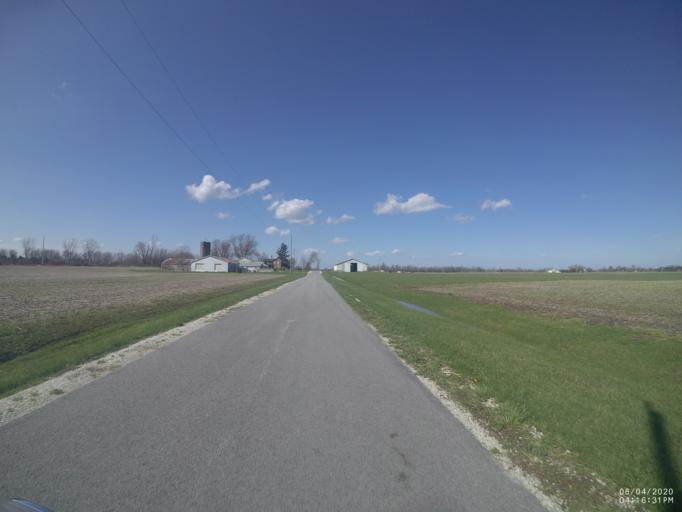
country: US
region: Ohio
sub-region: Sandusky County
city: Stony Prairie
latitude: 41.3018
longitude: -83.1924
